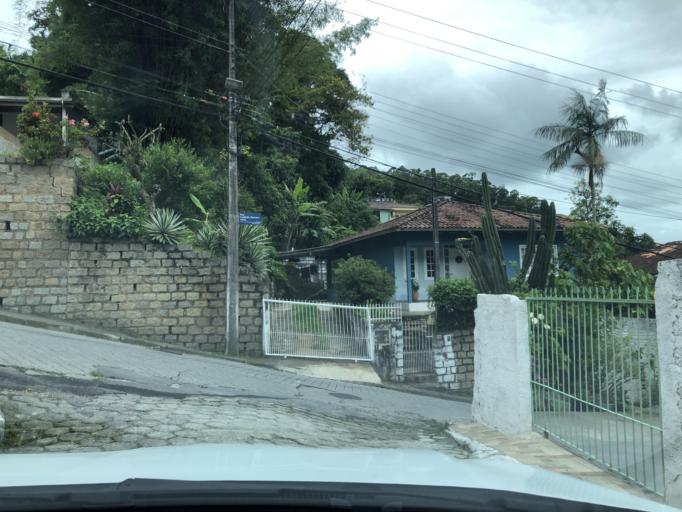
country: BR
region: Santa Catarina
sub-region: Florianopolis
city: Saco dos Limoes
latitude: -27.6017
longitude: -48.5363
